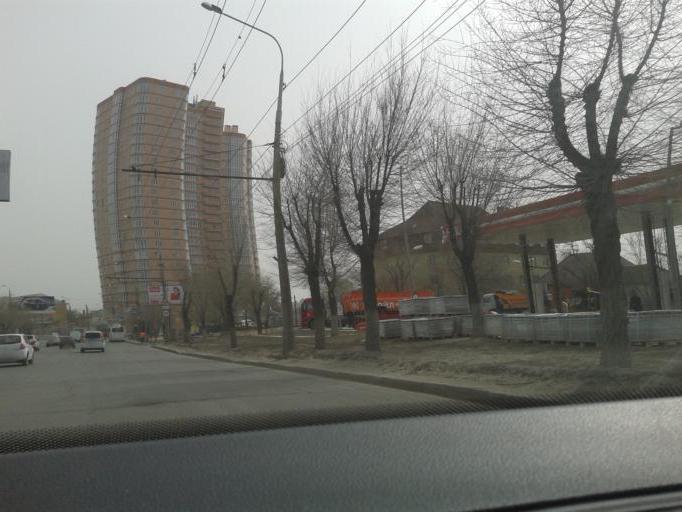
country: RU
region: Volgograd
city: Volgograd
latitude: 48.7230
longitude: 44.5024
